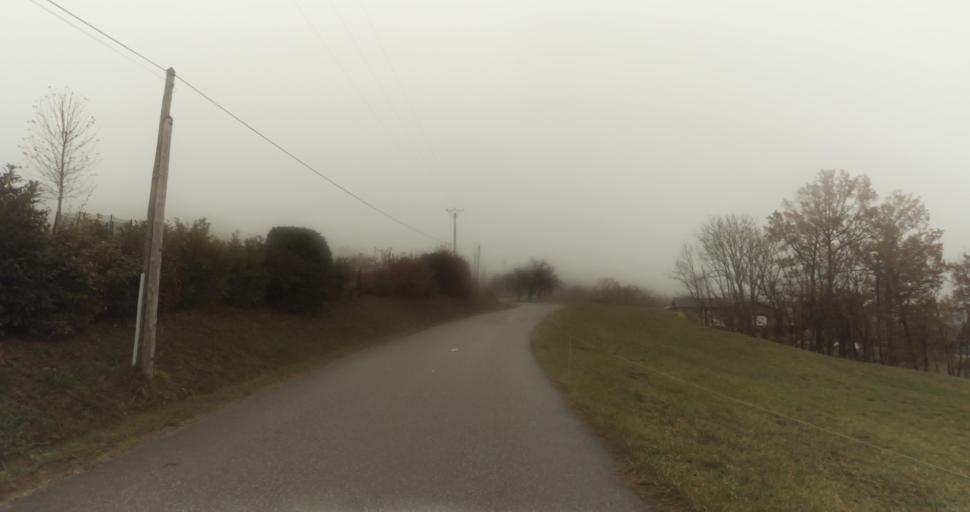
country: FR
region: Rhone-Alpes
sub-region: Departement de la Haute-Savoie
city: Villaz
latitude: 45.9764
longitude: 6.1827
